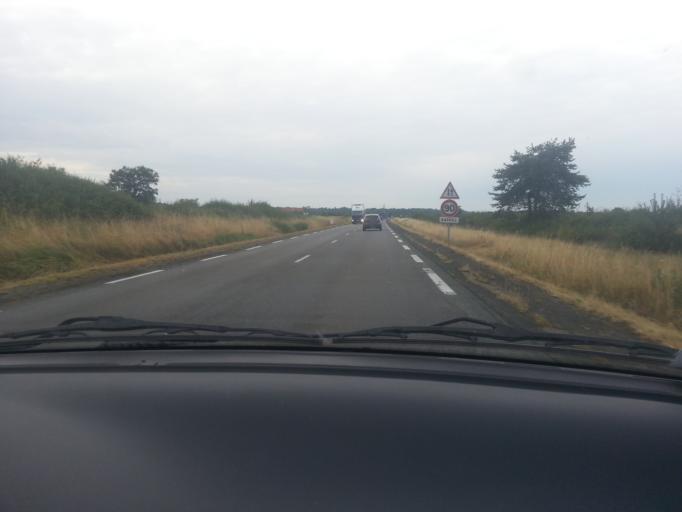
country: FR
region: Bourgogne
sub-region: Departement de Saone-et-Loire
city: Palinges
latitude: 46.5640
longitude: 4.1914
